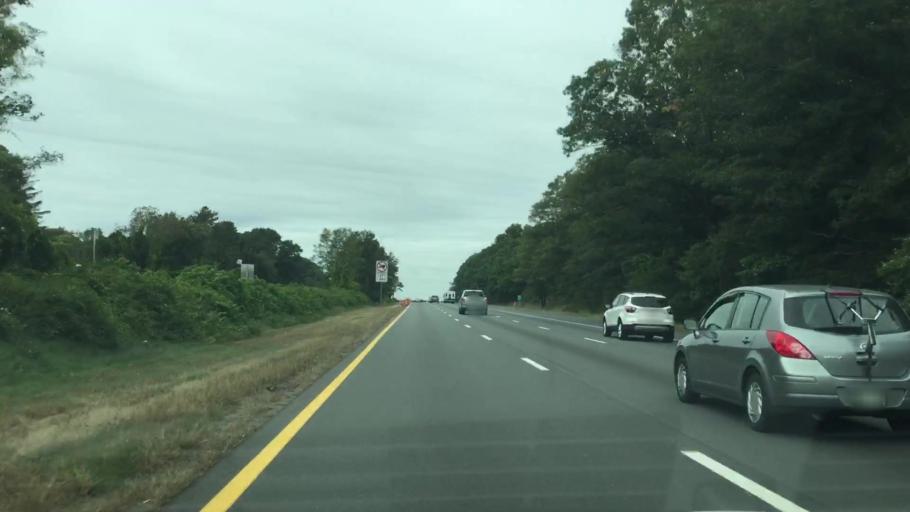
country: US
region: Massachusetts
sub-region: Essex County
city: Lawrence
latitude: 42.6773
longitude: -71.1604
